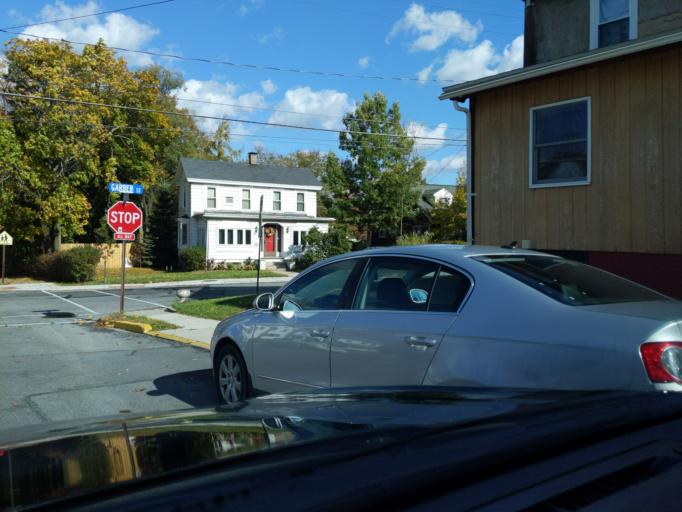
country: US
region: Pennsylvania
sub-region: Blair County
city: Hollidaysburg
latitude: 40.4342
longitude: -78.3950
